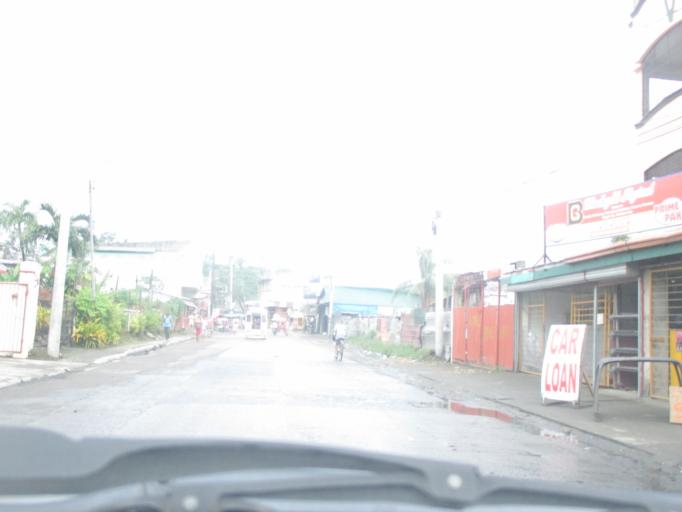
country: PH
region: Eastern Visayas
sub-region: Province of Leyte
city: Panalanoy
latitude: 11.2461
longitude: 124.9968
